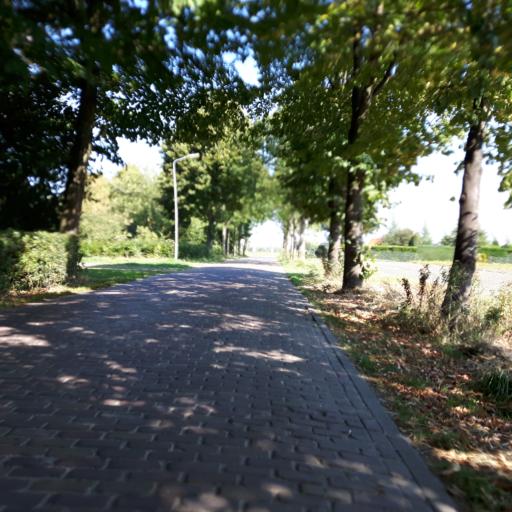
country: NL
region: Zeeland
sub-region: Gemeente Middelburg
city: Middelburg
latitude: 51.4535
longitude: 3.6284
